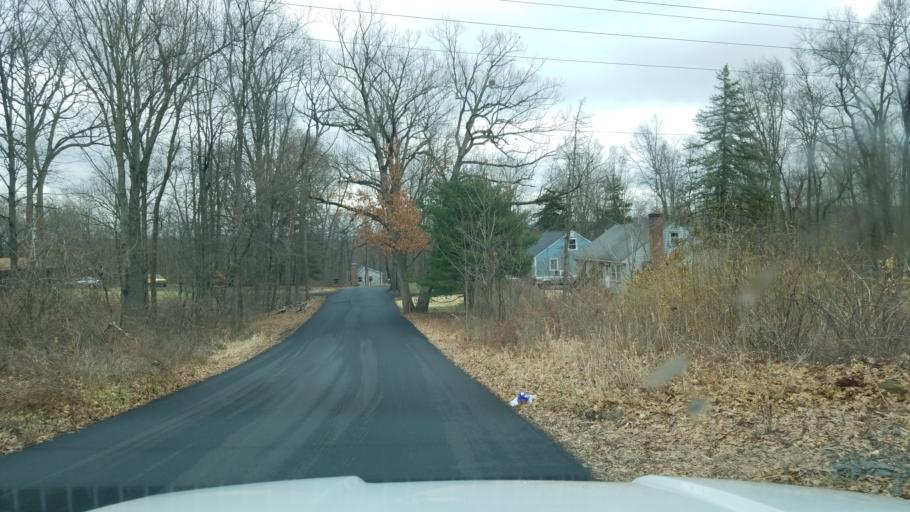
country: US
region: Connecticut
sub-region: Hartford County
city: Kensington
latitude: 41.6017
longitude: -72.7267
